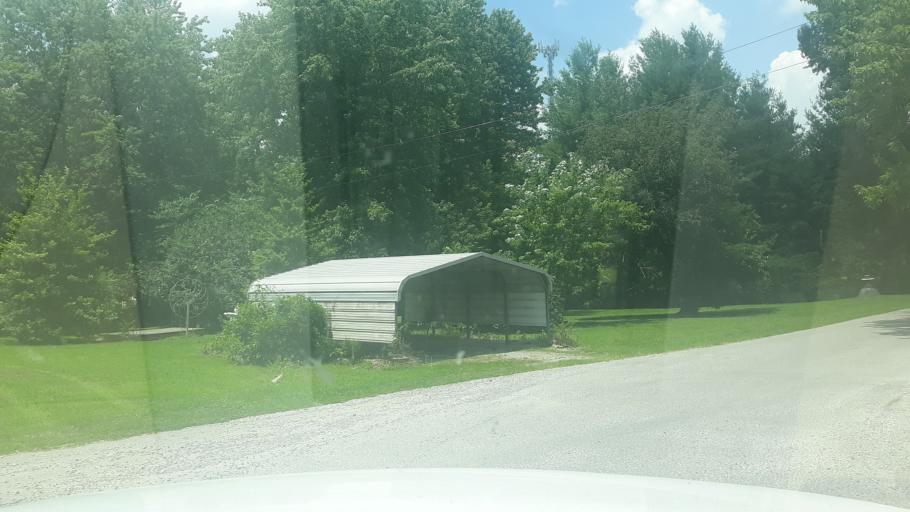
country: US
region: Illinois
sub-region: Saline County
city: Harrisburg
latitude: 37.7242
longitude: -88.5590
